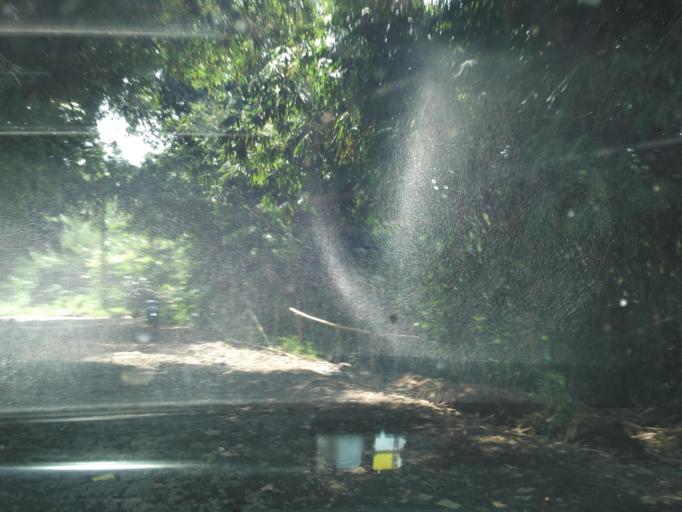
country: ID
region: West Java
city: Sukabumi
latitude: -6.8594
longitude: 107.0354
